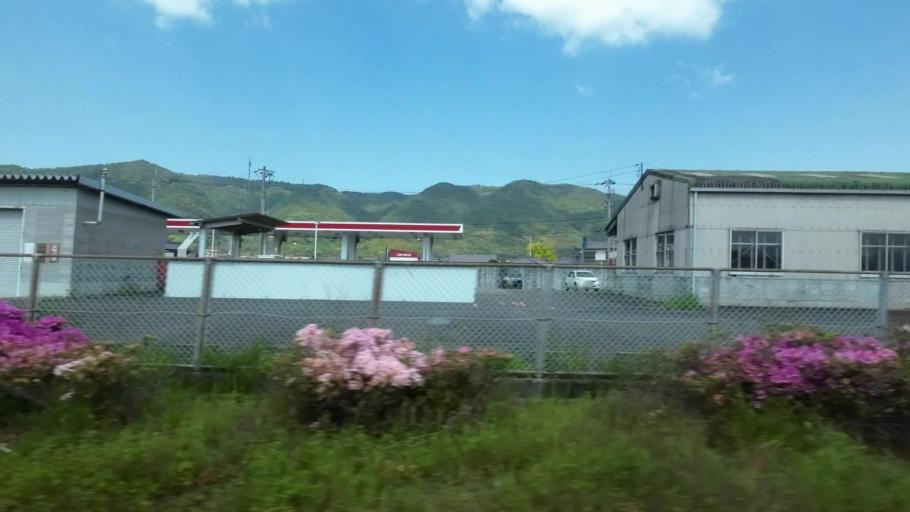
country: JP
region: Kagawa
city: Kan'onjicho
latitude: 34.1667
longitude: 133.6903
